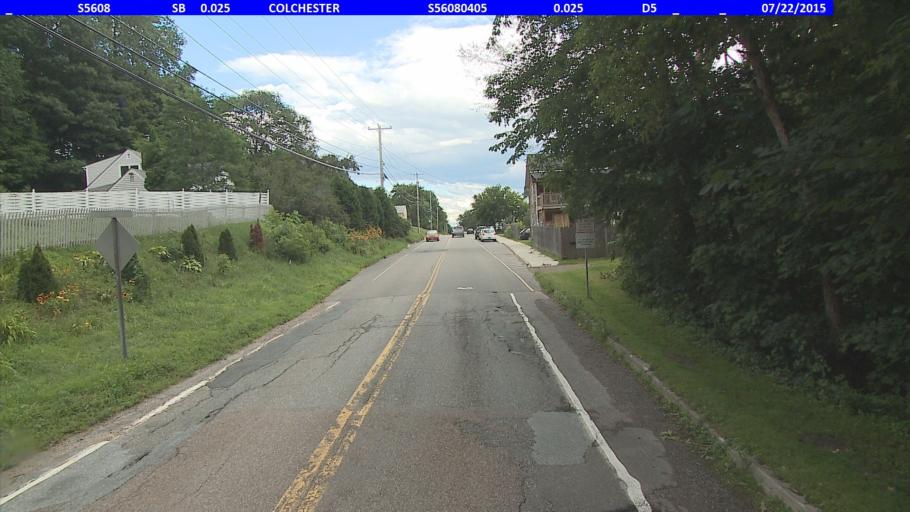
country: US
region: Vermont
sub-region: Chittenden County
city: Winooski
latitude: 44.4998
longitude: -73.1973
